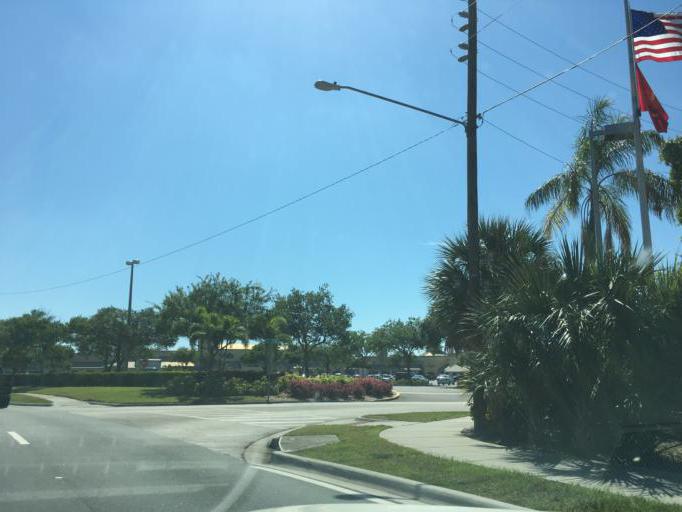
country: US
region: Florida
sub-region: Pinellas County
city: Lealman
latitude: 27.8068
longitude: -82.6374
